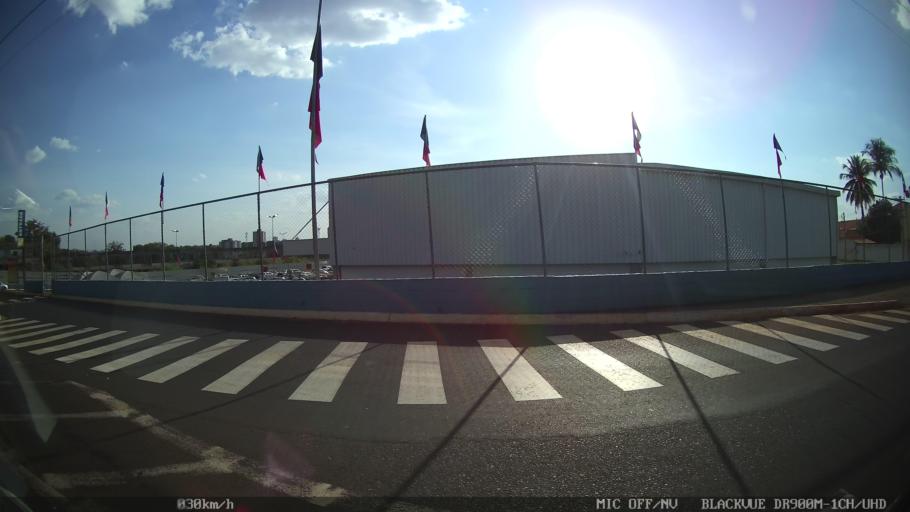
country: BR
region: Sao Paulo
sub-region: Ribeirao Preto
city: Ribeirao Preto
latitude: -21.1562
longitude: -47.8067
